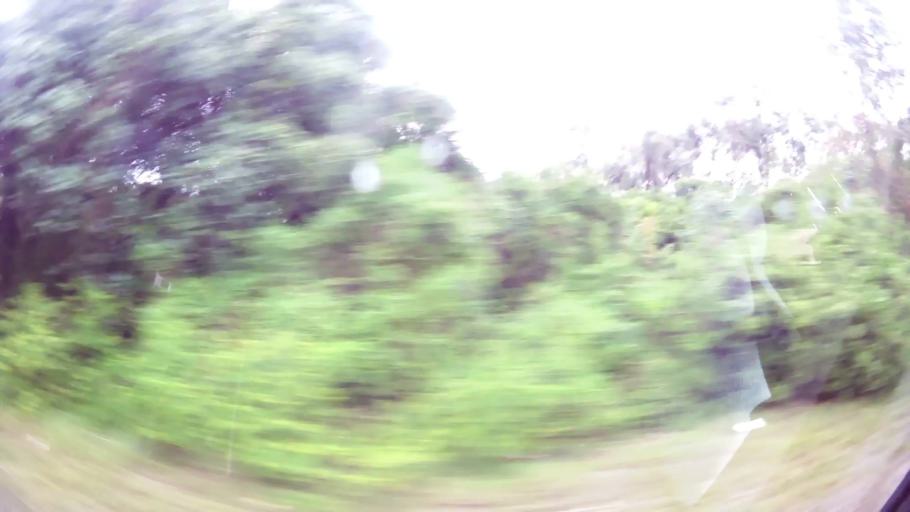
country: ZA
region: Eastern Cape
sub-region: Nelson Mandela Bay Metropolitan Municipality
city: Port Elizabeth
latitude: -34.0160
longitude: 25.5143
